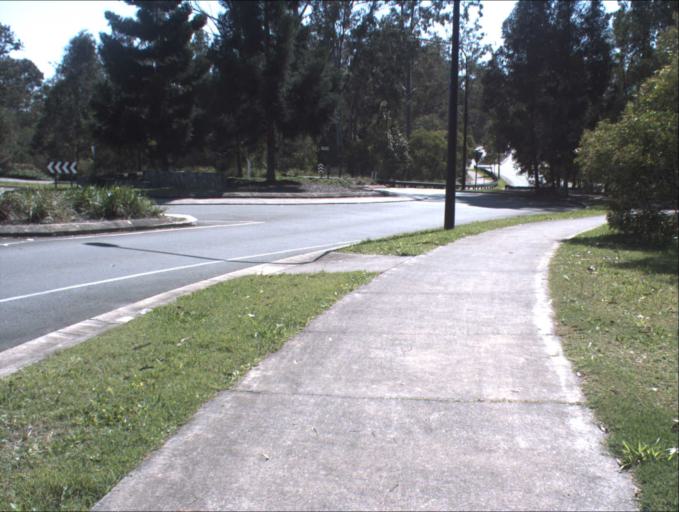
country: AU
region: Queensland
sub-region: Logan
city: Waterford West
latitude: -27.7173
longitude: 153.1452
